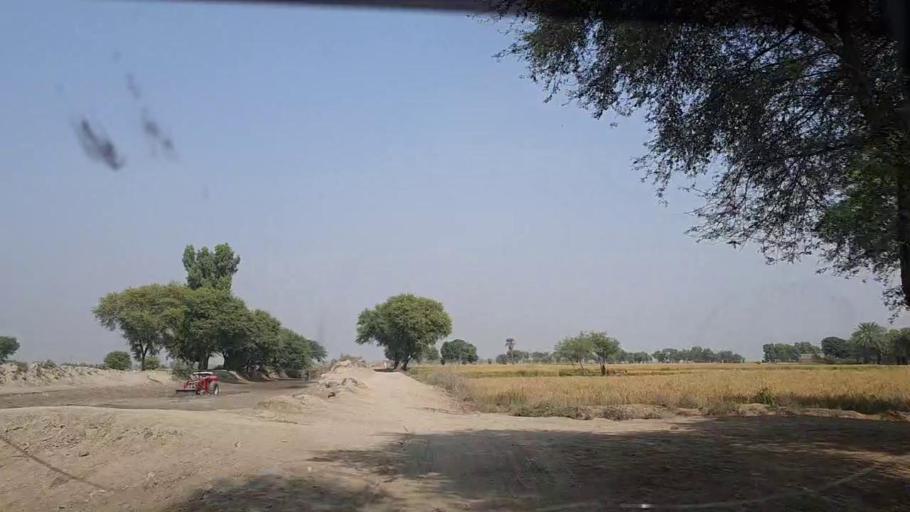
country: PK
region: Sindh
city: Thul
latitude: 28.1121
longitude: 68.6961
